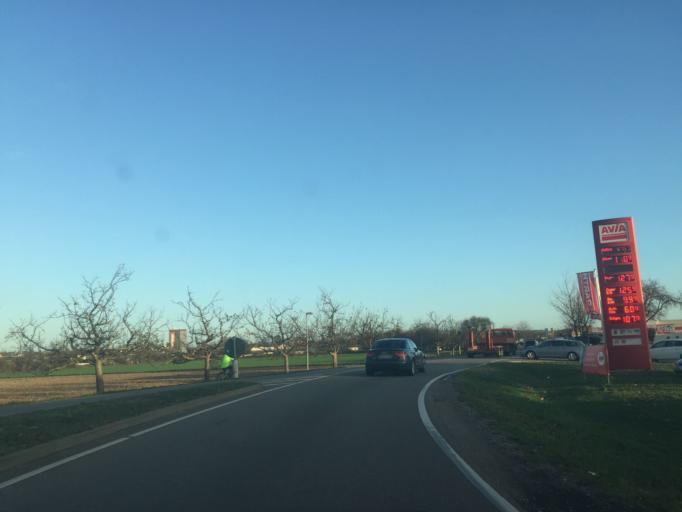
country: DE
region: Baden-Wuerttemberg
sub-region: Karlsruhe Region
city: Walldorf
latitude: 49.2941
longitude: 8.6557
